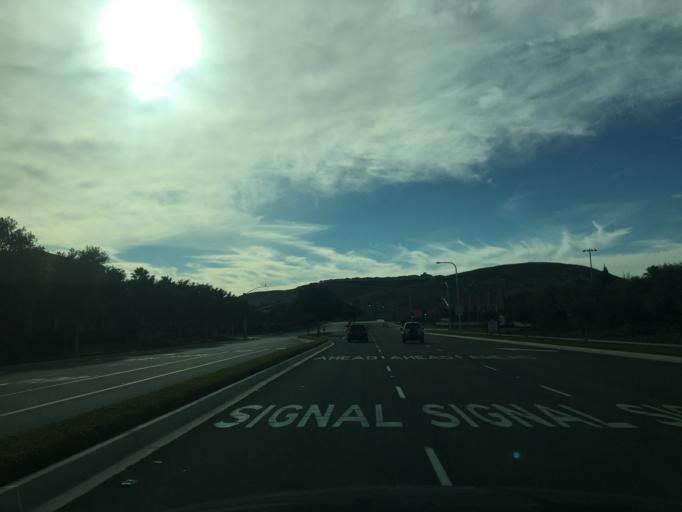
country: US
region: California
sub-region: Orange County
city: Laguna Woods
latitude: 33.6370
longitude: -117.7416
